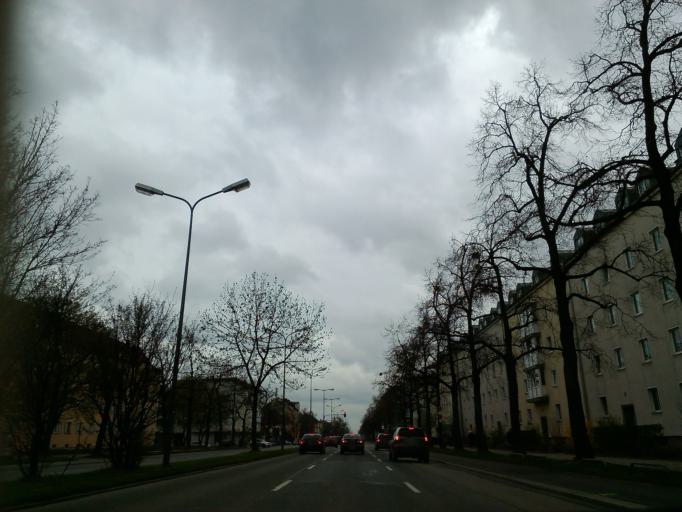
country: DE
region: Bavaria
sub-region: Upper Bavaria
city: Pasing
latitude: 48.1299
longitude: 11.5029
